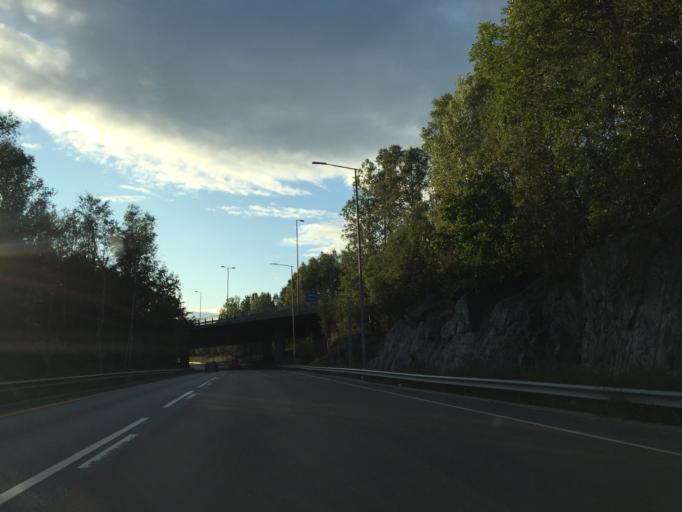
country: NO
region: Akershus
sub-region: Lorenskog
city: Kjenn
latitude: 59.9385
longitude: 10.9309
